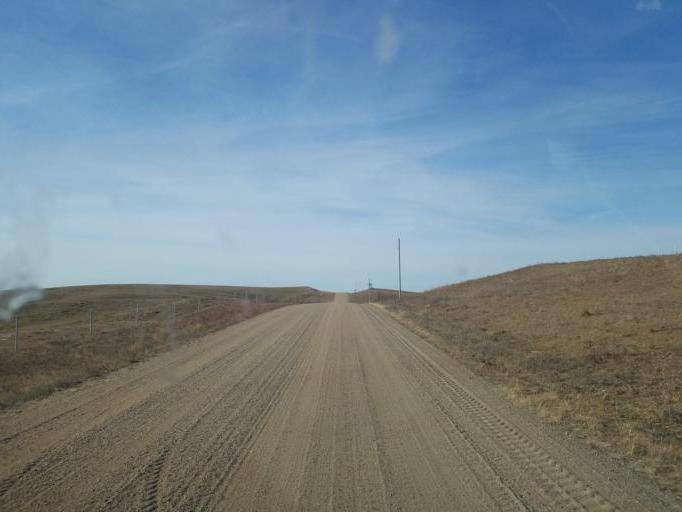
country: US
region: Nebraska
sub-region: Knox County
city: Center
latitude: 42.6261
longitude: -97.8290
